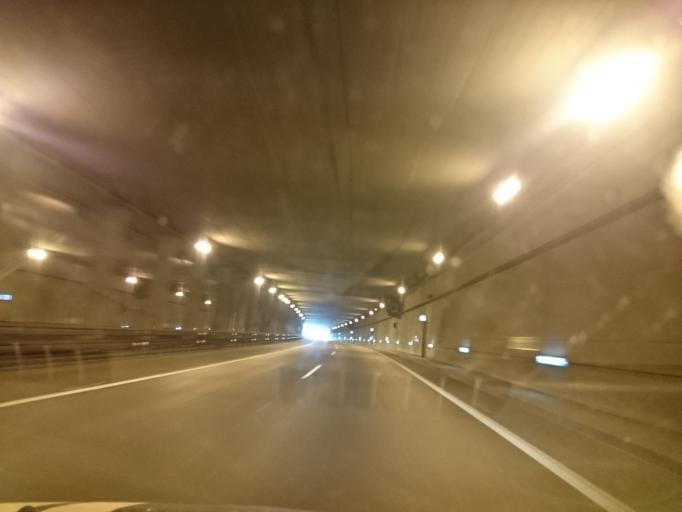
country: ES
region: Asturias
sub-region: Province of Asturias
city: Gijon
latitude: 43.5187
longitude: -5.6317
